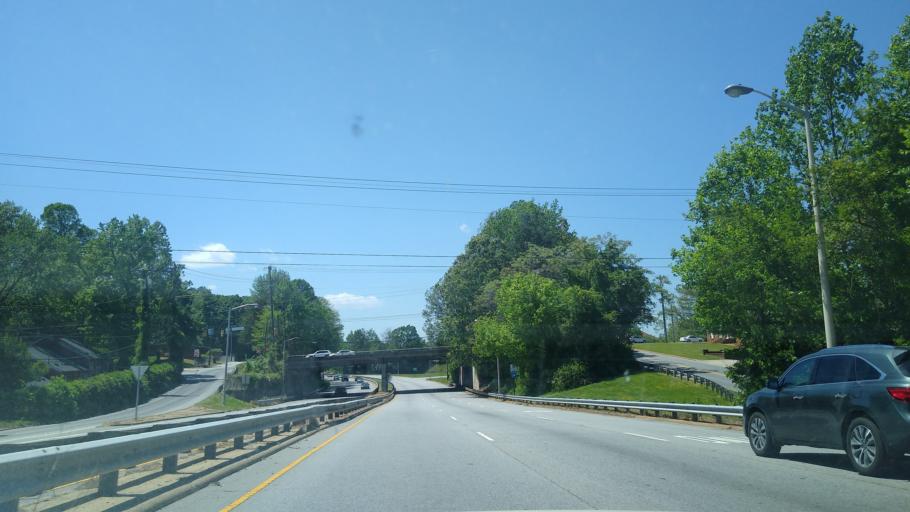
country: US
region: North Carolina
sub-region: Guilford County
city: Greensboro
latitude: 36.0883
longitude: -79.8121
